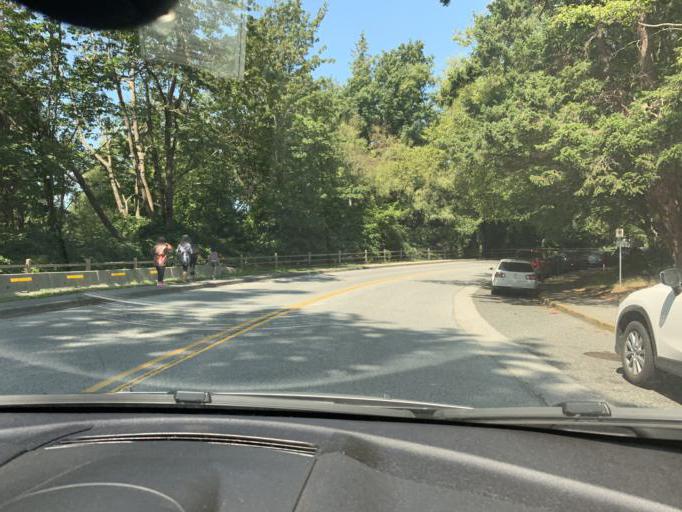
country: CA
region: British Columbia
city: West End
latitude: 49.2640
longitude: -123.2604
